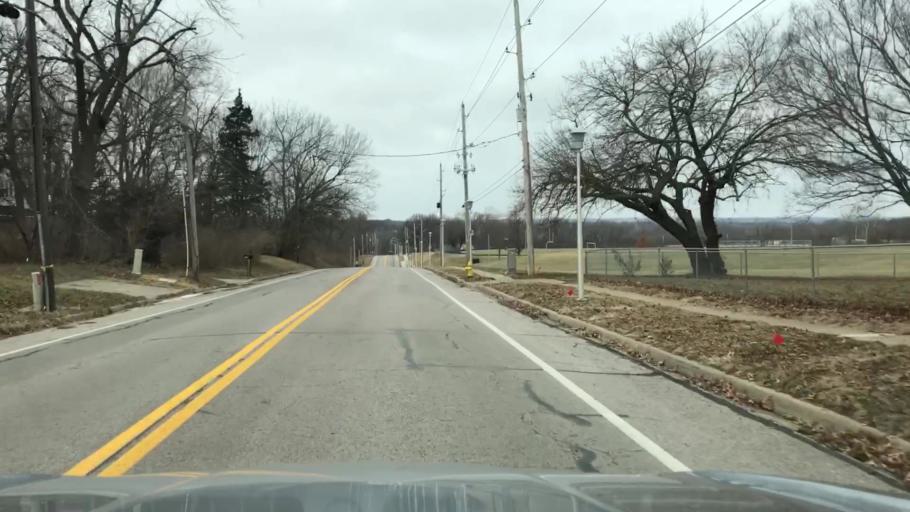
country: US
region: Missouri
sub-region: Jackson County
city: Lees Summit
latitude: 38.8965
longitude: -94.3865
